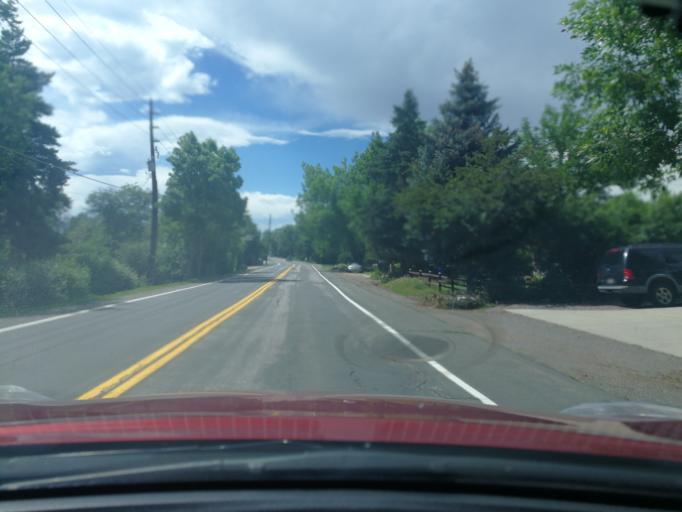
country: US
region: Colorado
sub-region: Arapahoe County
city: Littleton
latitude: 39.5944
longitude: -105.0032
